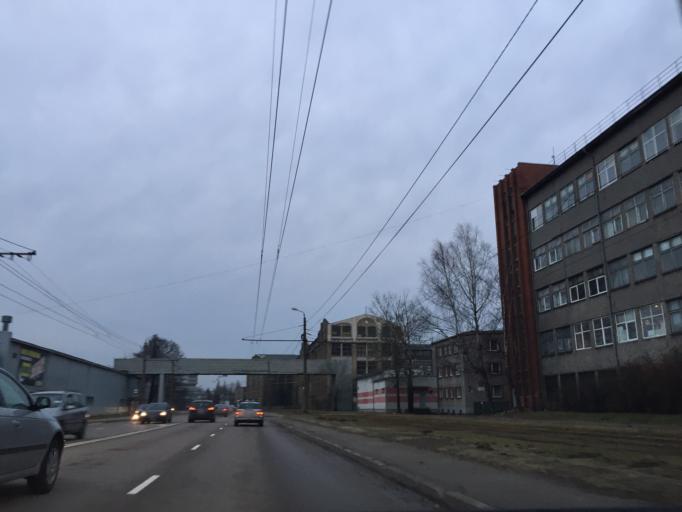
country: LV
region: Riga
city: Riga
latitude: 56.9844
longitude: 24.1198
